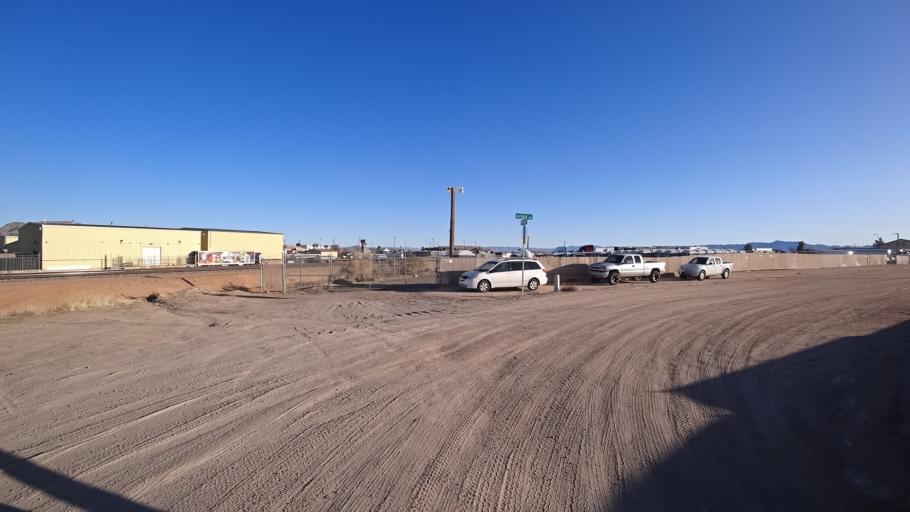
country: US
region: Arizona
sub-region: Mohave County
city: Kingman
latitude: 35.2103
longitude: -114.0136
